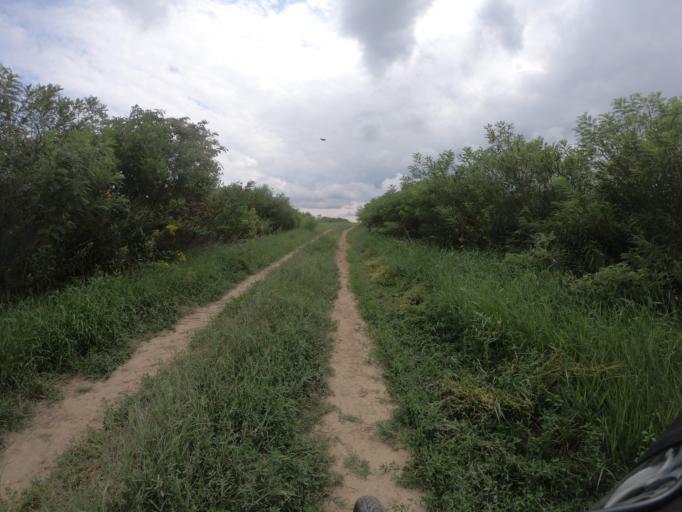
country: HU
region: Jasz-Nagykun-Szolnok
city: Tiszafured
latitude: 47.7044
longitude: 20.7763
